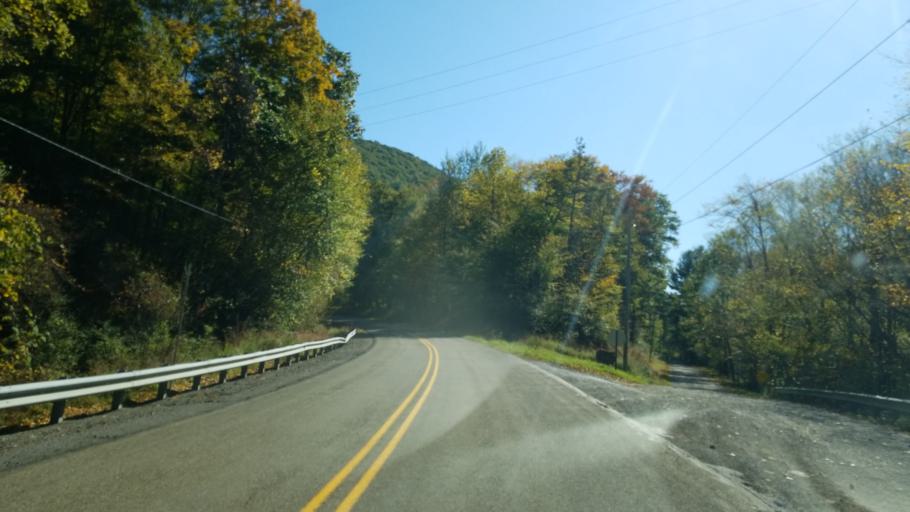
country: US
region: Pennsylvania
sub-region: Elk County
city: Saint Marys
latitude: 41.2694
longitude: -78.4032
